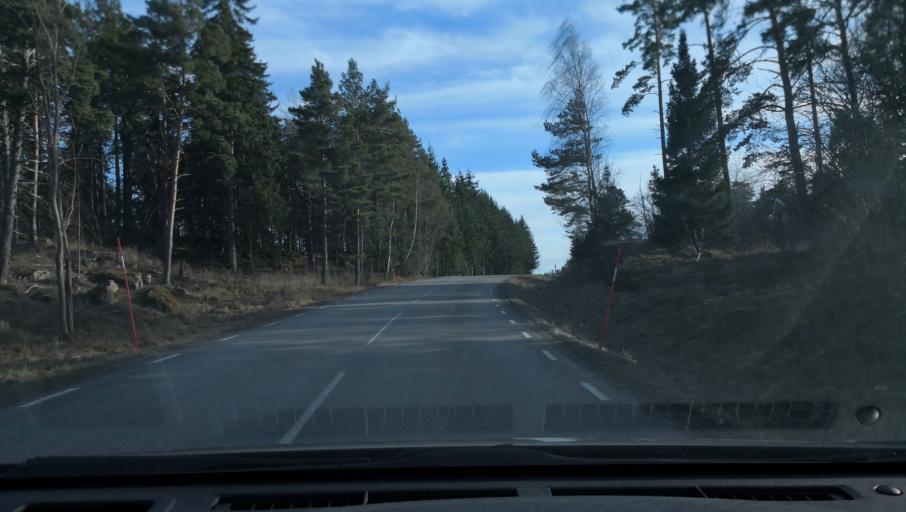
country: SE
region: Uppsala
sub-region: Enkopings Kommun
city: Enkoping
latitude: 59.6202
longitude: 17.0997
